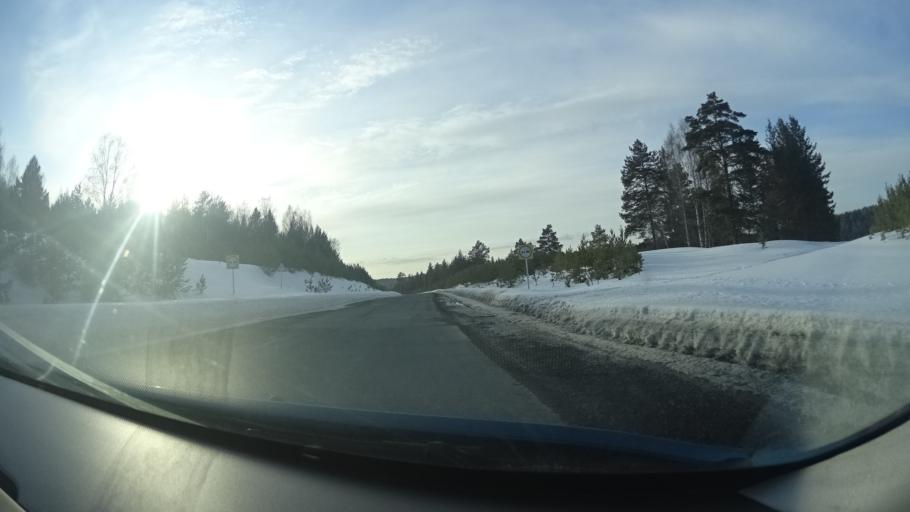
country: RU
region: Bashkortostan
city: Lomovka
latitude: 53.6718
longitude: 58.2359
